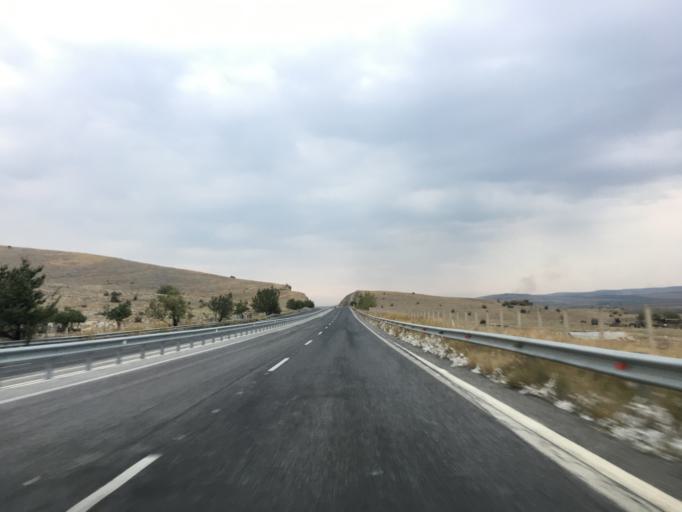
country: GR
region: Thessaly
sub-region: Trikala
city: Zarkos
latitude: 39.6098
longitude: 22.2361
